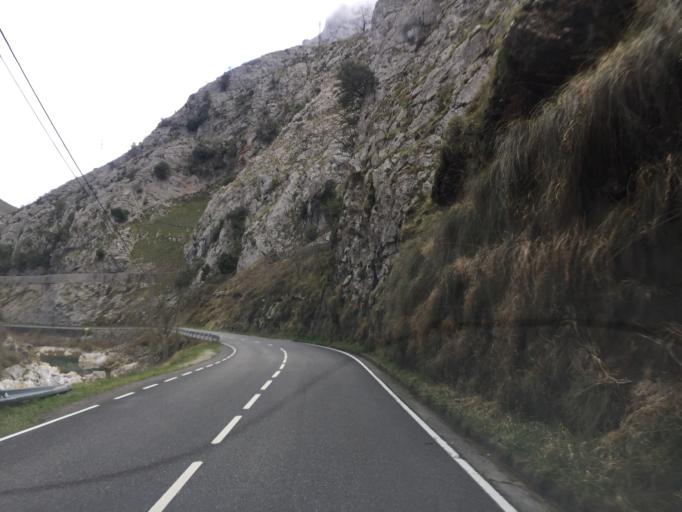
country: ES
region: Asturias
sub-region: Province of Asturias
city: Carrena
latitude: 43.2684
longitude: -4.8312
